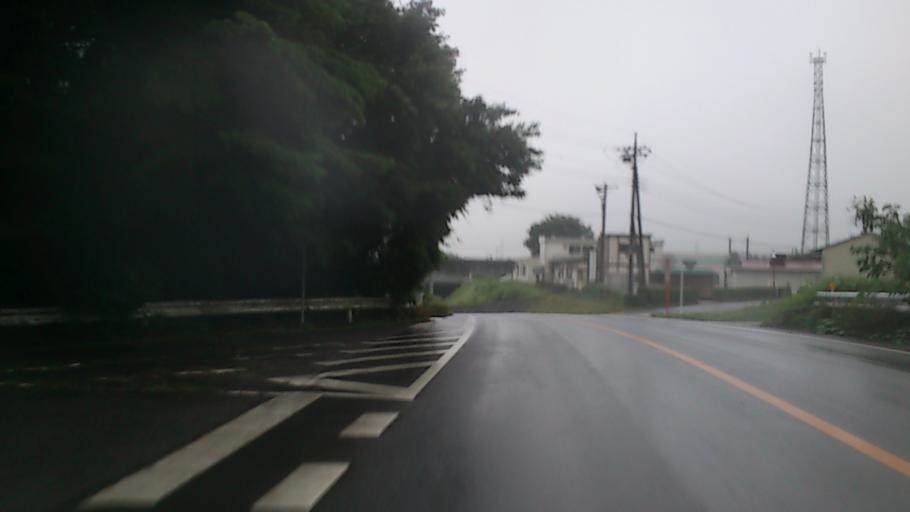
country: JP
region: Tochigi
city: Otawara
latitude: 36.9035
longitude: 139.9968
